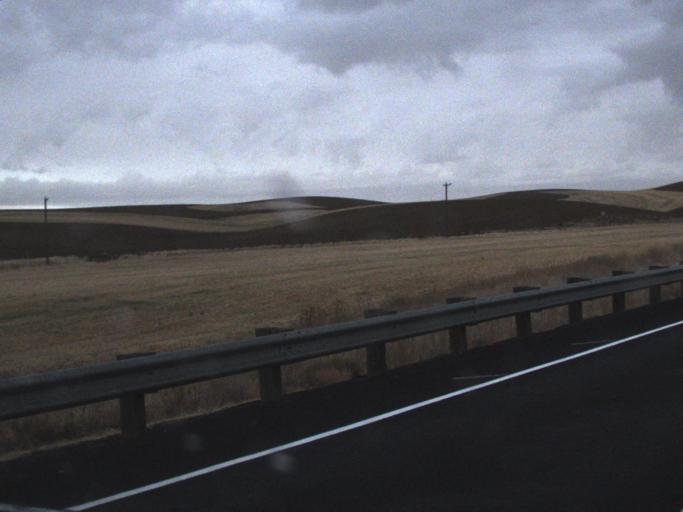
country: US
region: Washington
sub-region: Garfield County
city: Pomeroy
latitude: 46.8053
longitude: -117.8342
